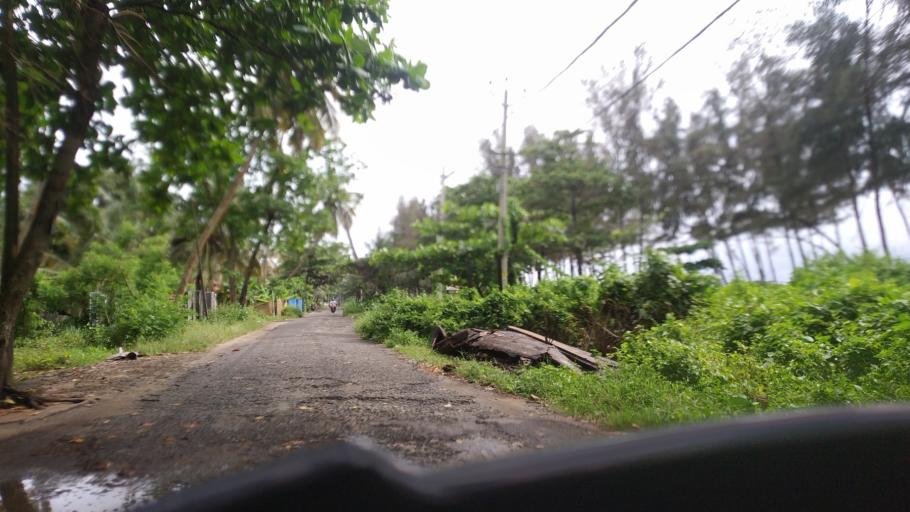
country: IN
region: Kerala
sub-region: Thrissur District
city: Kodungallur
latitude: 10.1274
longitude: 76.1831
